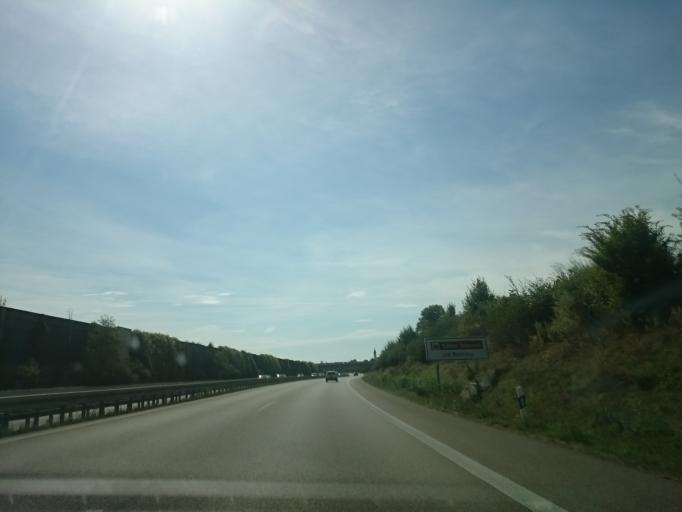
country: DE
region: Bavaria
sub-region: Swabia
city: Langweid
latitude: 48.4979
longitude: 10.8601
